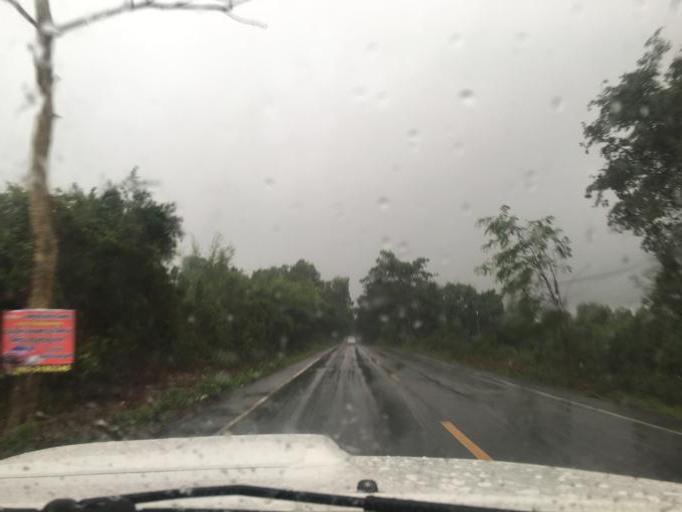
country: TH
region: Changwat Udon Thani
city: Udon Thani
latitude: 17.3411
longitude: 102.7169
